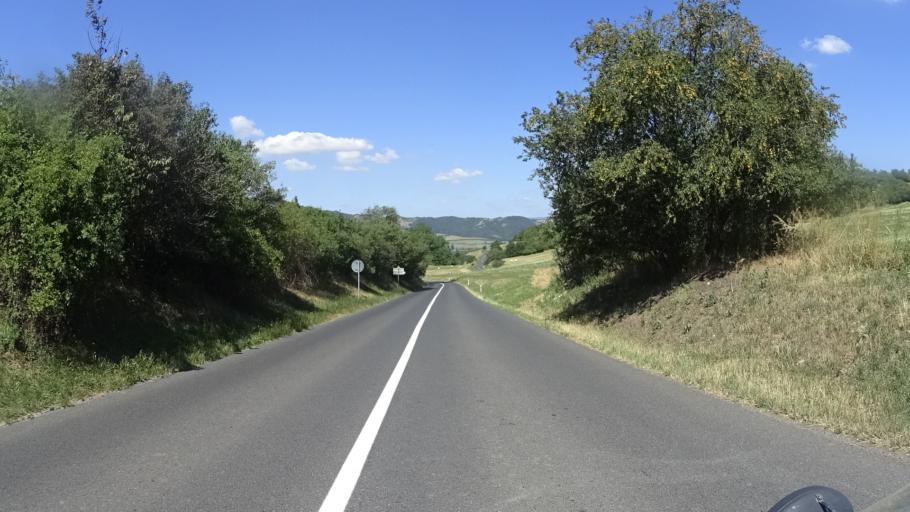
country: CZ
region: Ustecky
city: Lovosice
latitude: 50.5567
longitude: 14.0695
